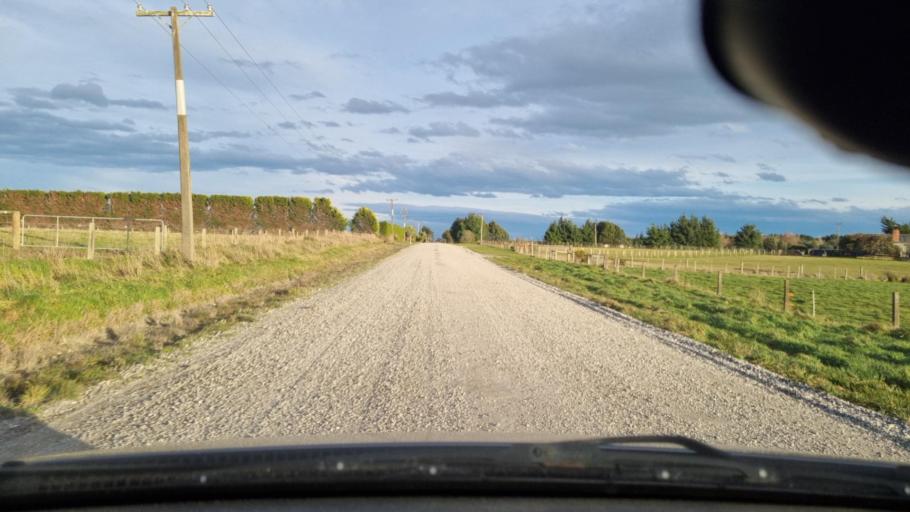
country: NZ
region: Southland
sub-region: Invercargill City
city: Invercargill
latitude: -46.3705
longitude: 168.2985
